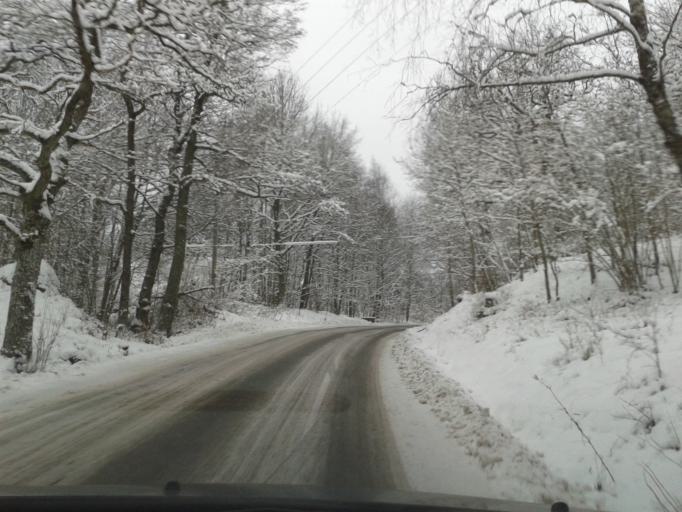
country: SE
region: Stockholm
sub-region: Nacka Kommun
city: Saltsjobaden
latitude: 59.2214
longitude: 18.3042
